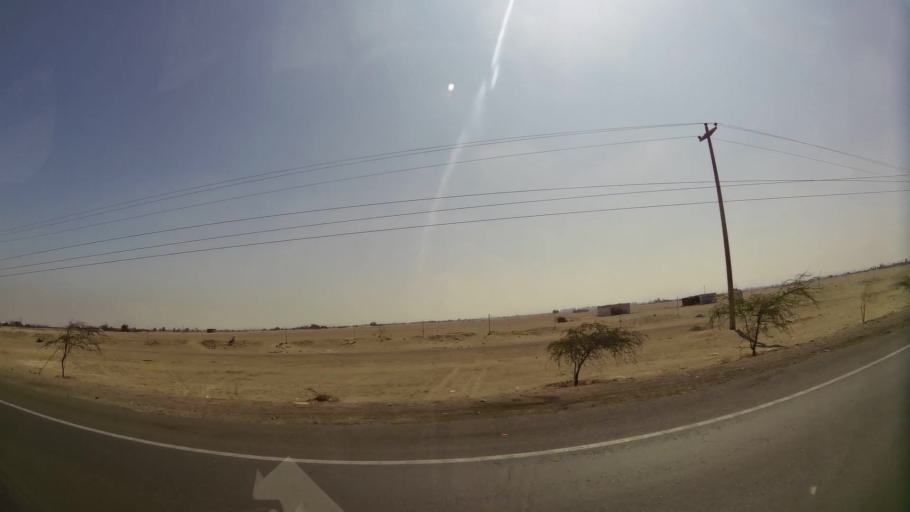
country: PE
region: Ica
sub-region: Provincia de Ica
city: Guadalupe
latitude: -13.9312
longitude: -75.9295
